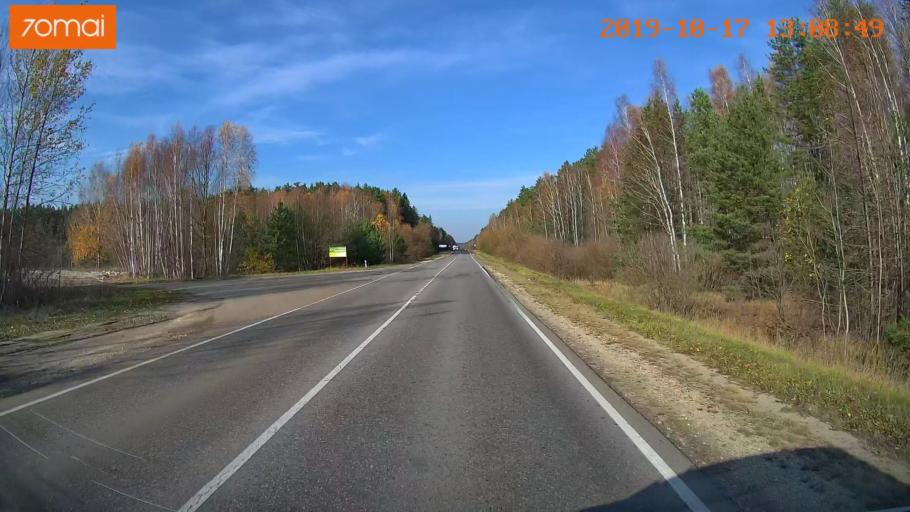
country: RU
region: Rjazan
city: Syntul
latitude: 54.9943
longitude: 41.2669
